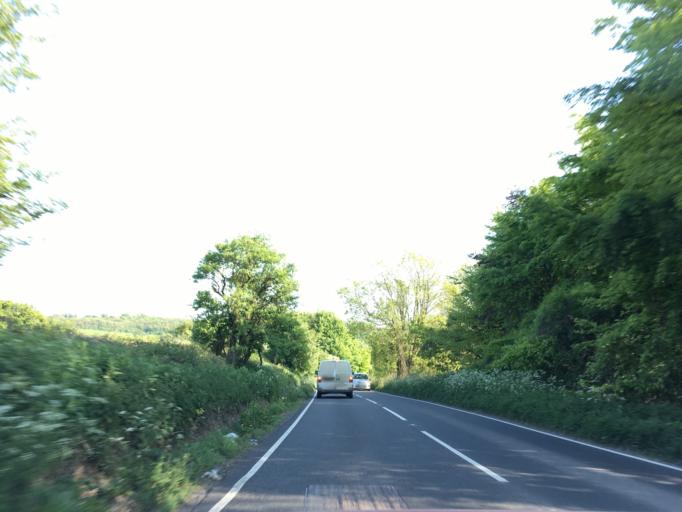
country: GB
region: England
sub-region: Gloucestershire
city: Wotton-under-Edge
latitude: 51.6517
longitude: -2.3366
